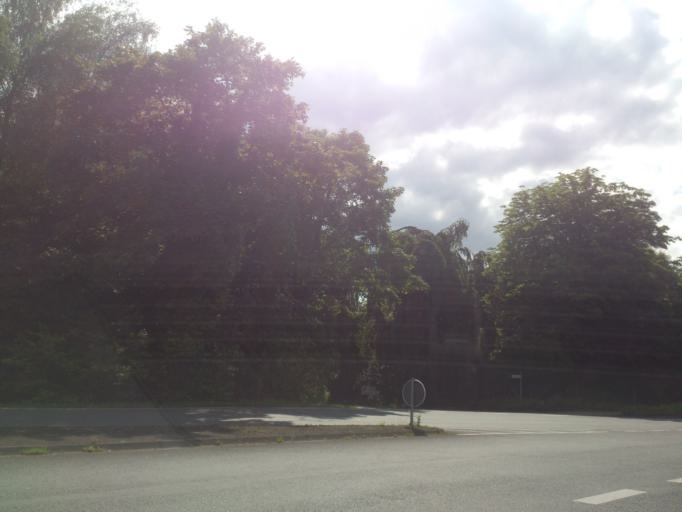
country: DE
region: North Rhine-Westphalia
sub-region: Regierungsbezirk Detmold
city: Steinhagen
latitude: 51.9851
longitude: 8.3486
